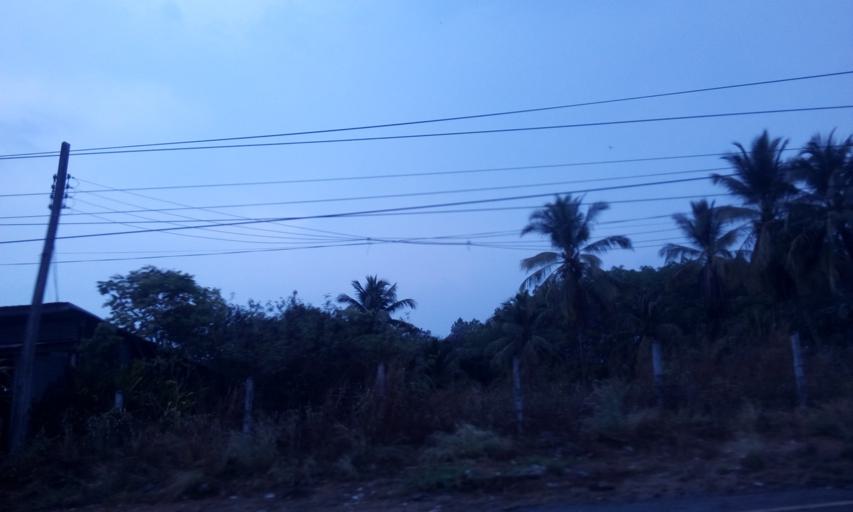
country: TH
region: Trat
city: Khao Saming
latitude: 12.3632
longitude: 102.3846
